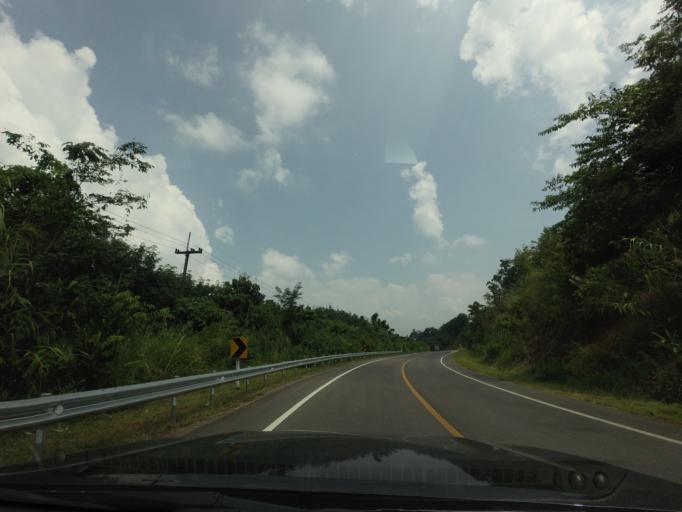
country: TH
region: Nan
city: Santi Suk
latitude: 18.9251
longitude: 100.8945
